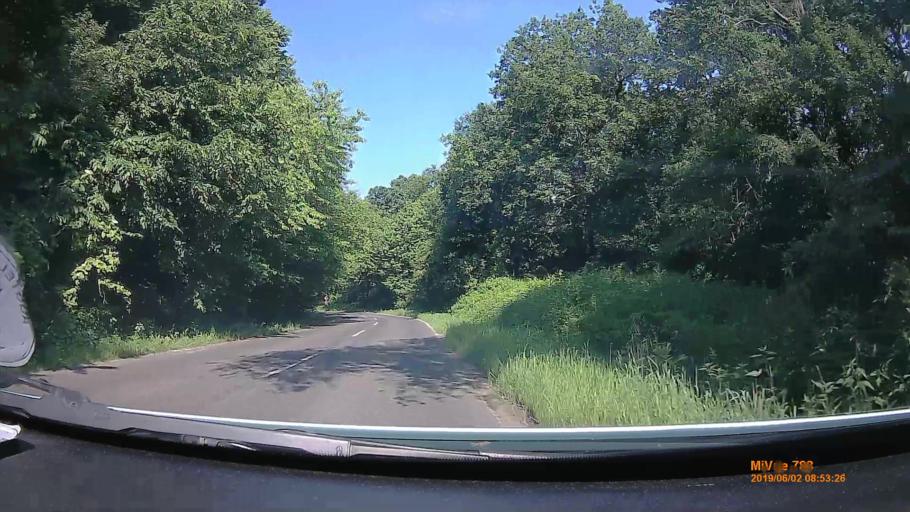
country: HU
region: Borsod-Abauj-Zemplen
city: Sajobabony
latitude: 48.1513
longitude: 20.6805
